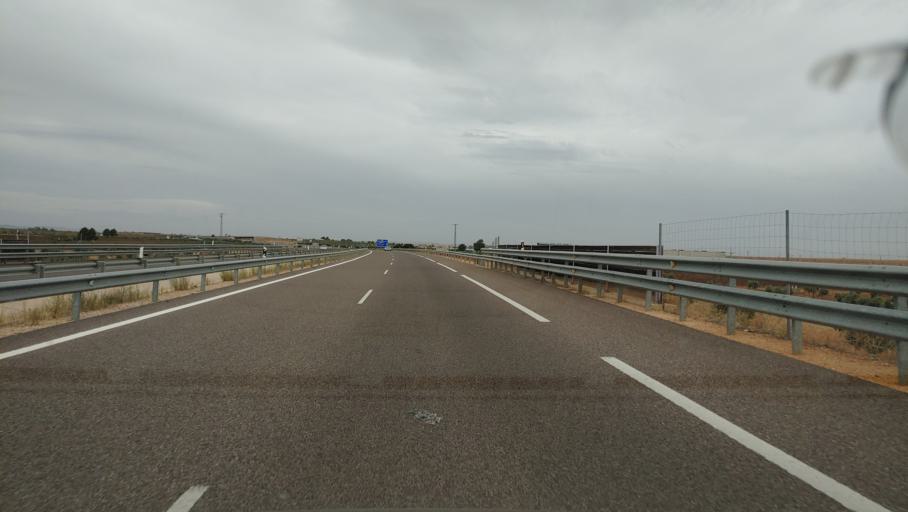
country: ES
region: Castille-La Mancha
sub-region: Provincia de Ciudad Real
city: Valenzuela de Calatrava
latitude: 38.9020
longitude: -3.8005
